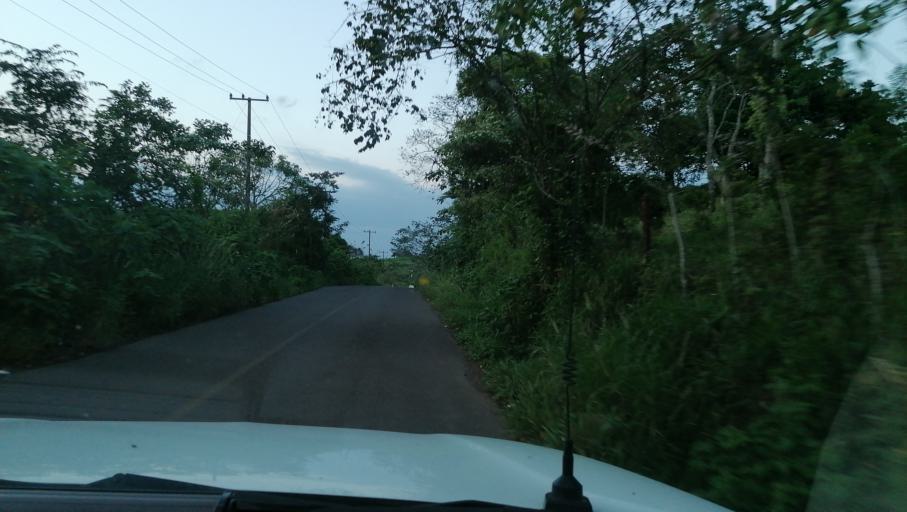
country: MX
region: Chiapas
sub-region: Ostuacan
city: Nuevo Juan del Grijalva
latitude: 17.4342
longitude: -93.3508
